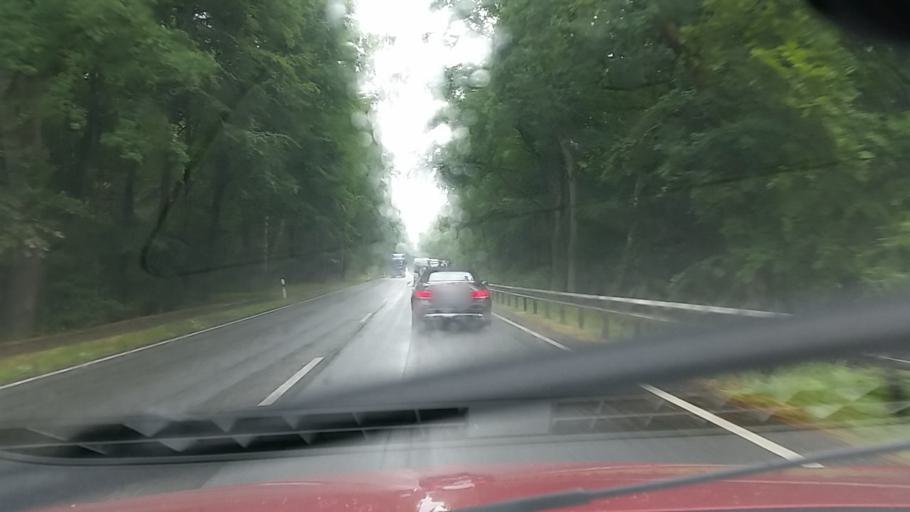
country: DE
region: Lower Saxony
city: Suderburg
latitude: 52.8795
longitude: 10.5007
